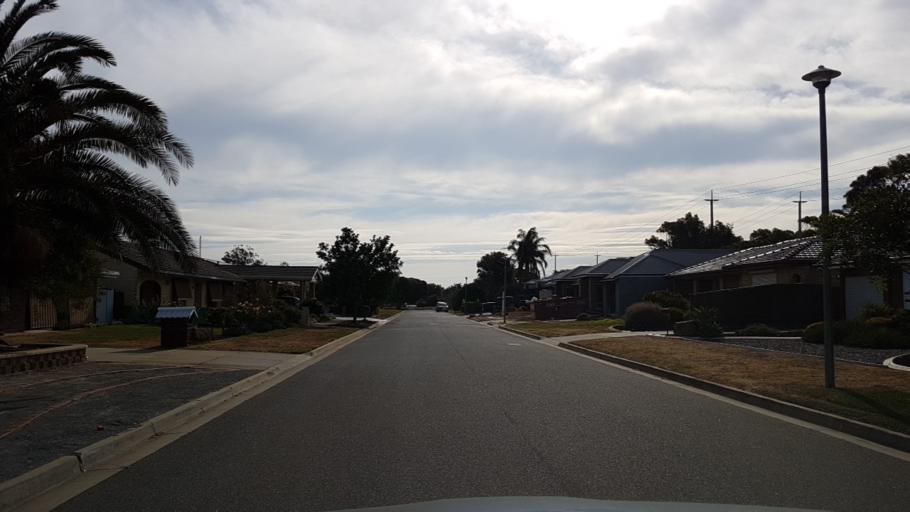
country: AU
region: South Australia
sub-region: Charles Sturt
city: West Lakes Shore
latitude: -34.8579
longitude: 138.4926
